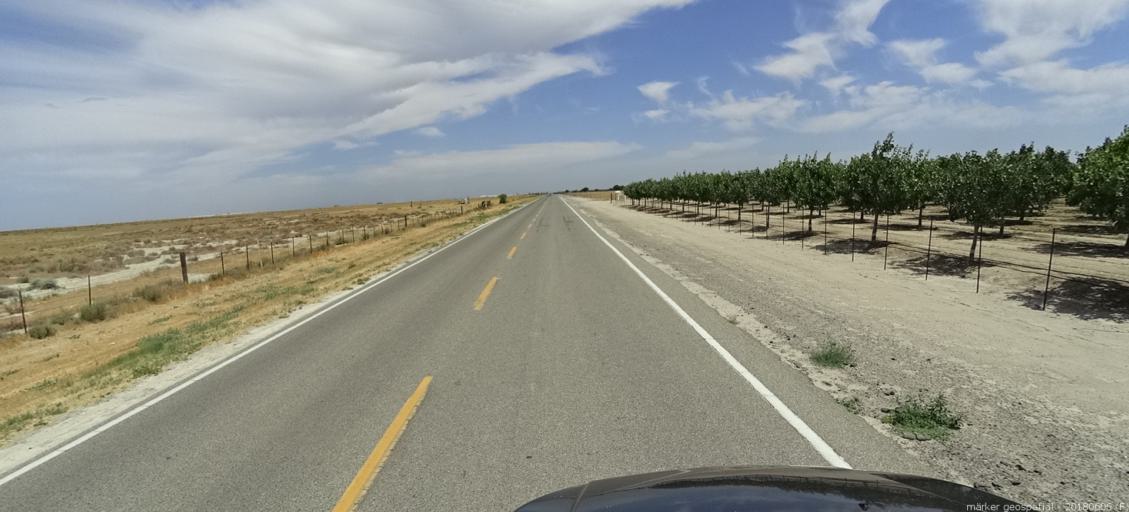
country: US
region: California
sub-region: Fresno County
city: Firebaugh
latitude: 36.8938
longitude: -120.3819
